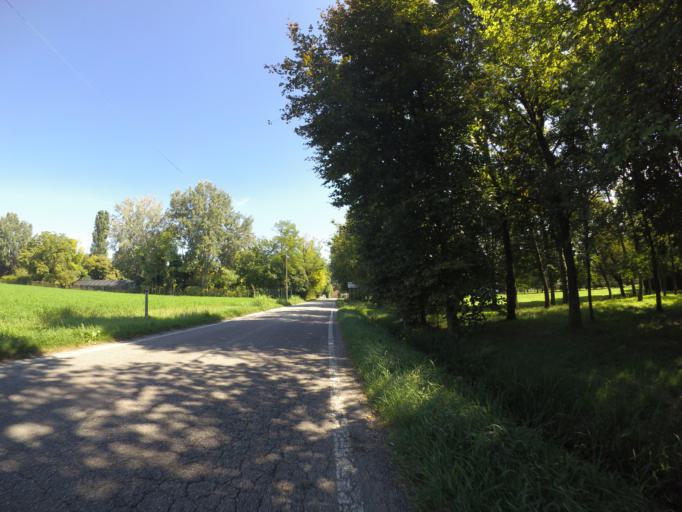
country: IT
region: Friuli Venezia Giulia
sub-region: Provincia di Udine
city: Varmo
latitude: 45.9009
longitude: 12.9760
